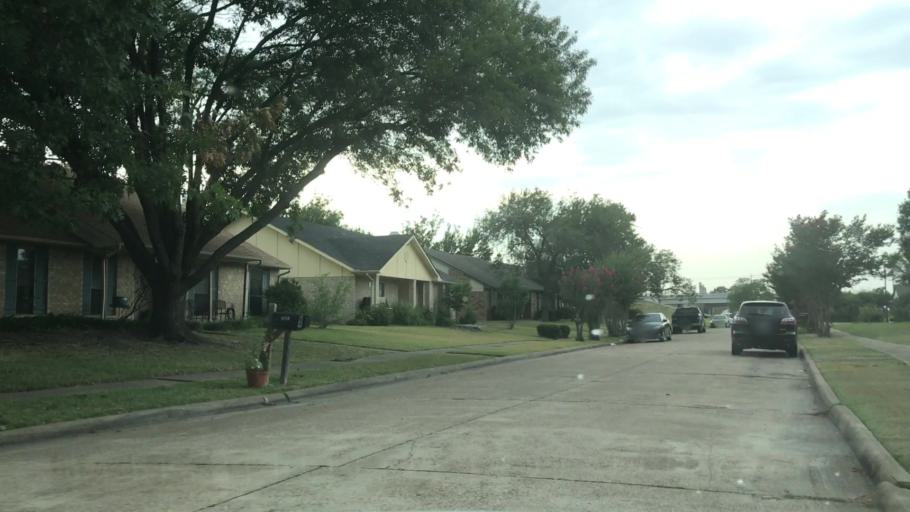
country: US
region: Texas
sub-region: Dallas County
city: Rowlett
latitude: 32.8516
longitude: -96.5600
